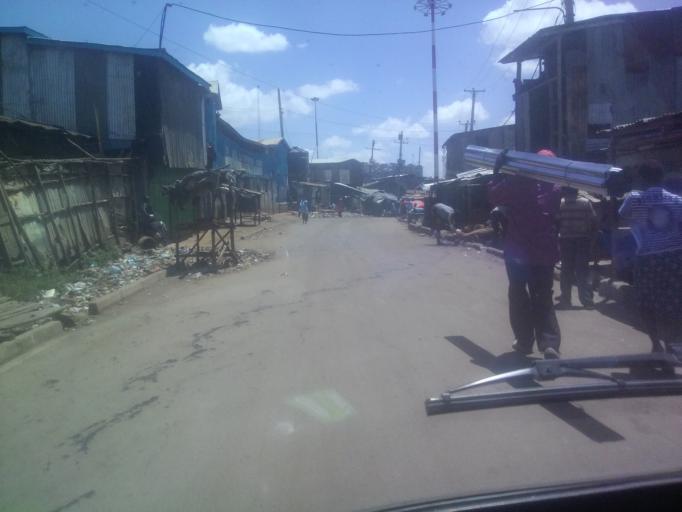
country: KE
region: Nairobi Area
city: Nairobi
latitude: -1.3153
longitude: 36.7984
